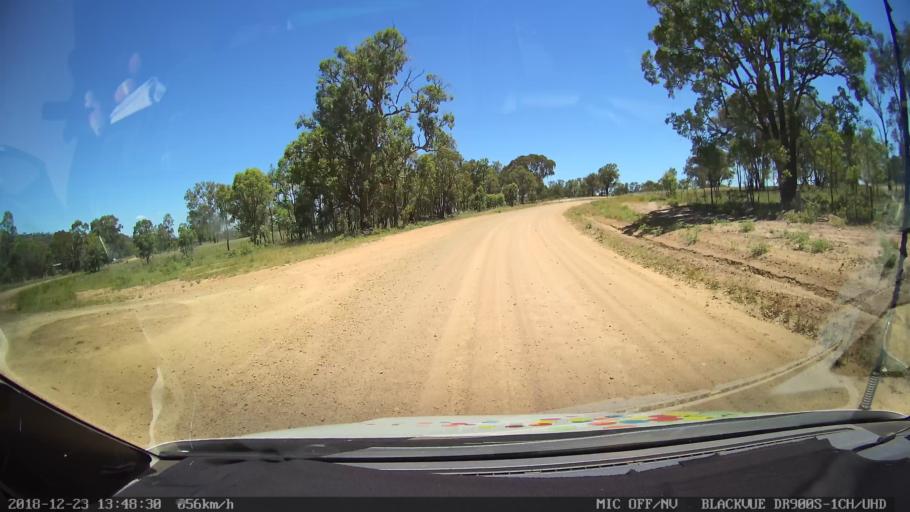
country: AU
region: New South Wales
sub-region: Tamworth Municipality
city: Manilla
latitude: -30.5180
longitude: 151.1163
